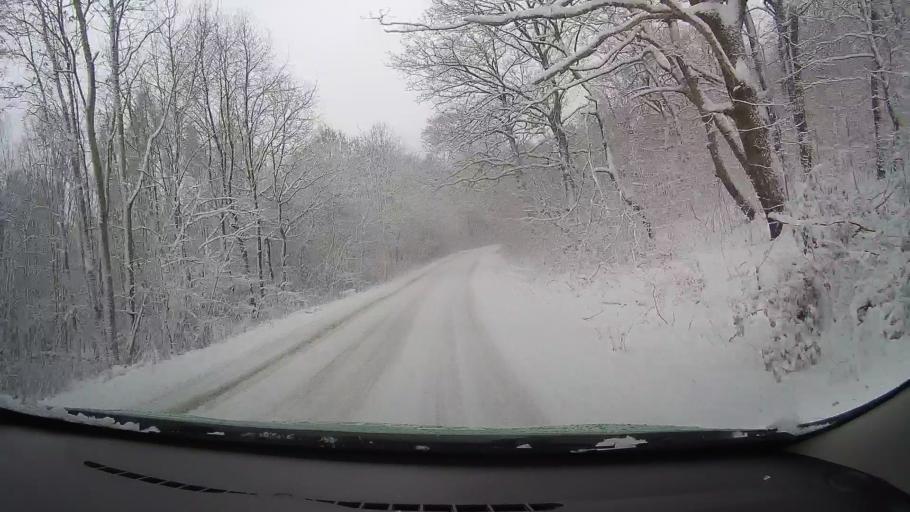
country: RO
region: Hunedoara
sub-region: Municipiul Deva
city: Deva
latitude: 45.8510
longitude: 22.8791
